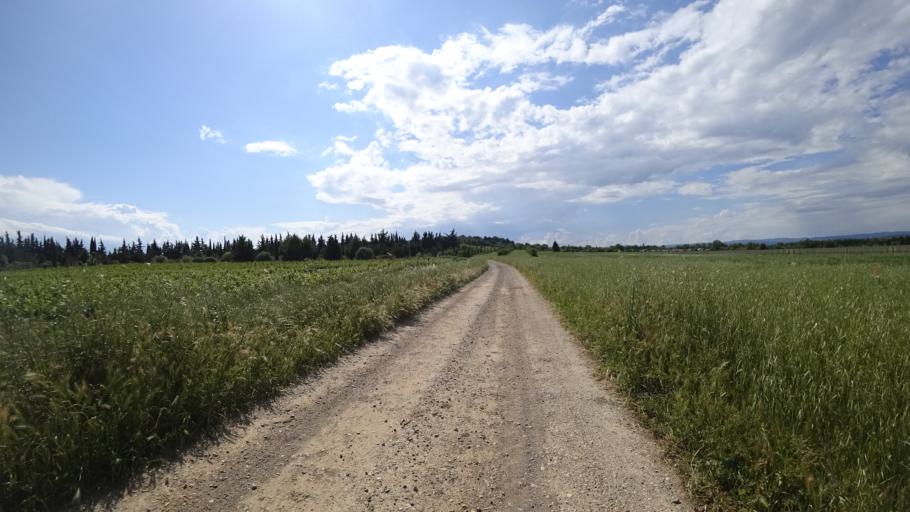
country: FR
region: Languedoc-Roussillon
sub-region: Departement de l'Aude
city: Ginestas
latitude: 43.2623
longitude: 2.8855
